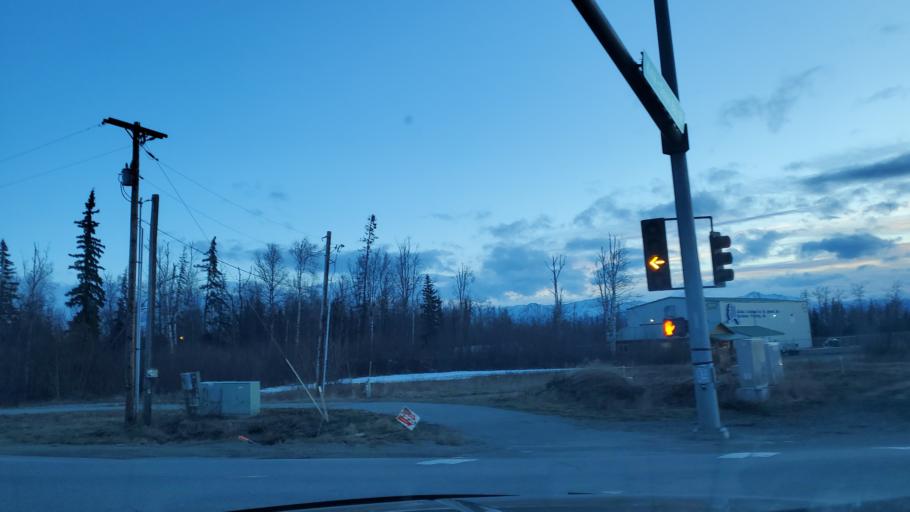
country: US
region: Alaska
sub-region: Matanuska-Susitna Borough
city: Wasilla
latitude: 61.5706
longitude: -149.4447
